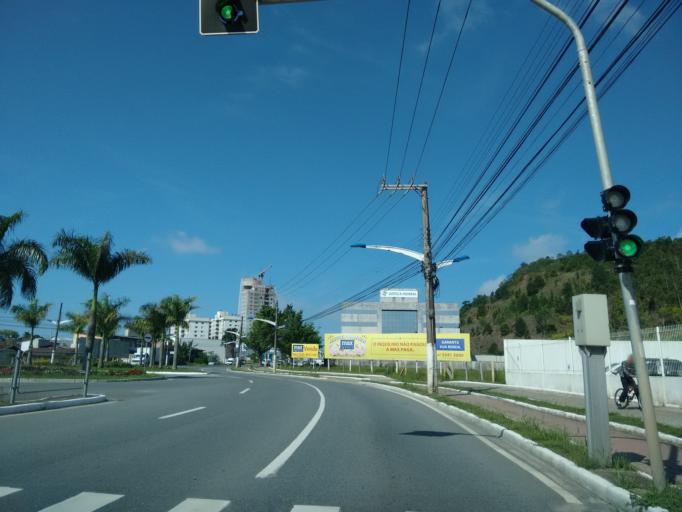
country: BR
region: Santa Catarina
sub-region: Itajai
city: Itajai
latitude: -26.9296
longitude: -48.6845
